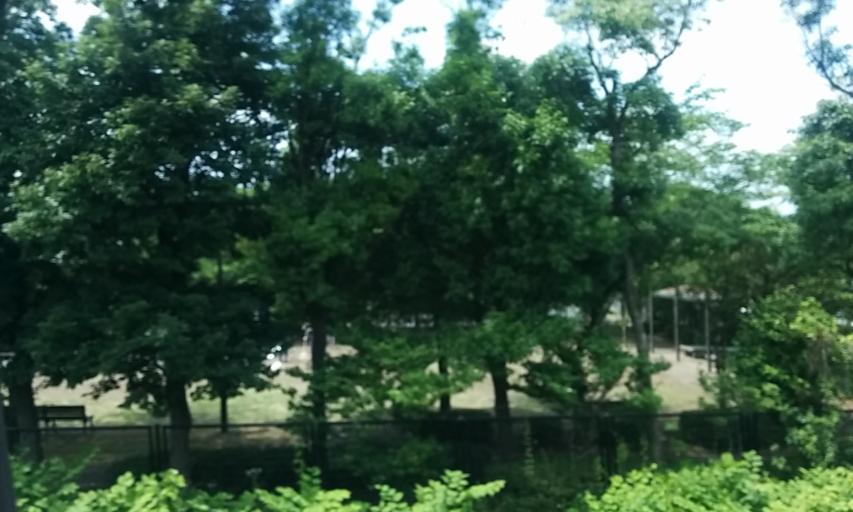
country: JP
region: Chiba
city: Sakura
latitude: 35.7286
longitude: 140.2180
